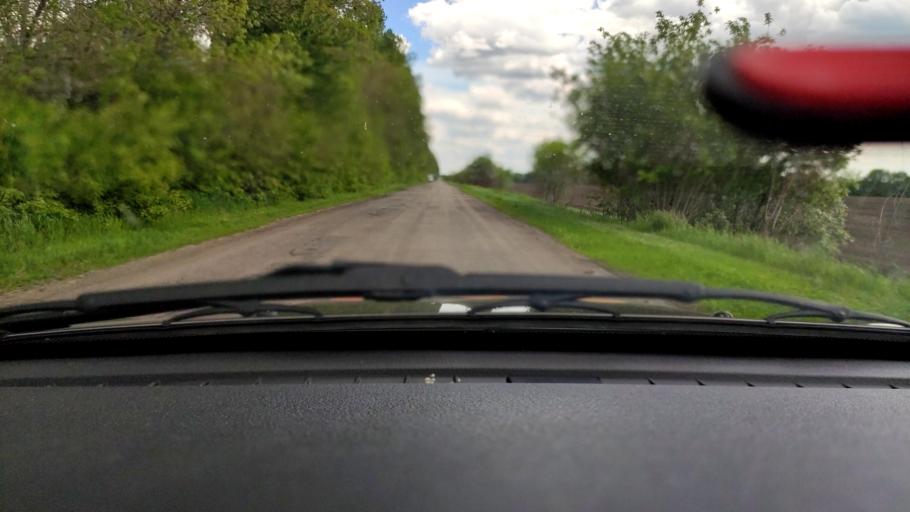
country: RU
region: Voronezj
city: Uryv-Pokrovka
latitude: 51.1290
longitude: 39.1061
